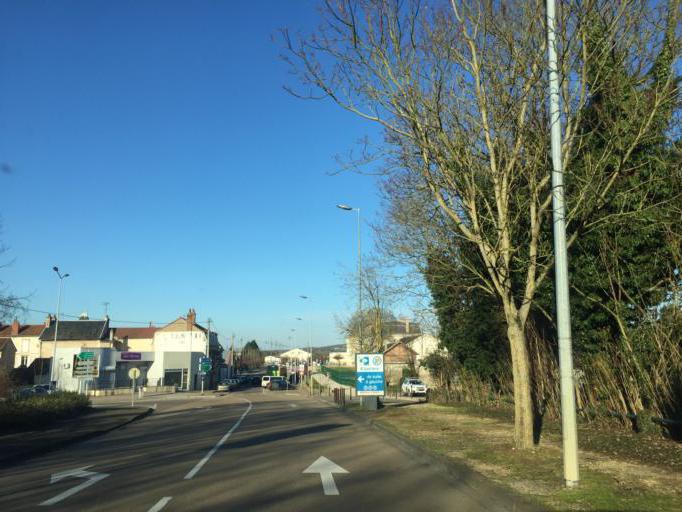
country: FR
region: Bourgogne
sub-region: Departement de l'Yonne
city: Auxerre
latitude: 47.7955
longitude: 3.5843
